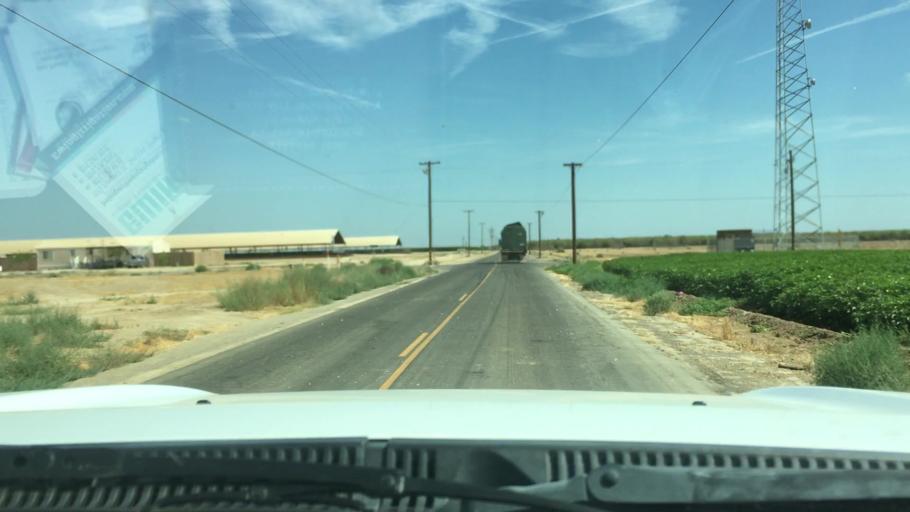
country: US
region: California
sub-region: Kern County
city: Shafter
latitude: 35.4703
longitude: -119.3680
